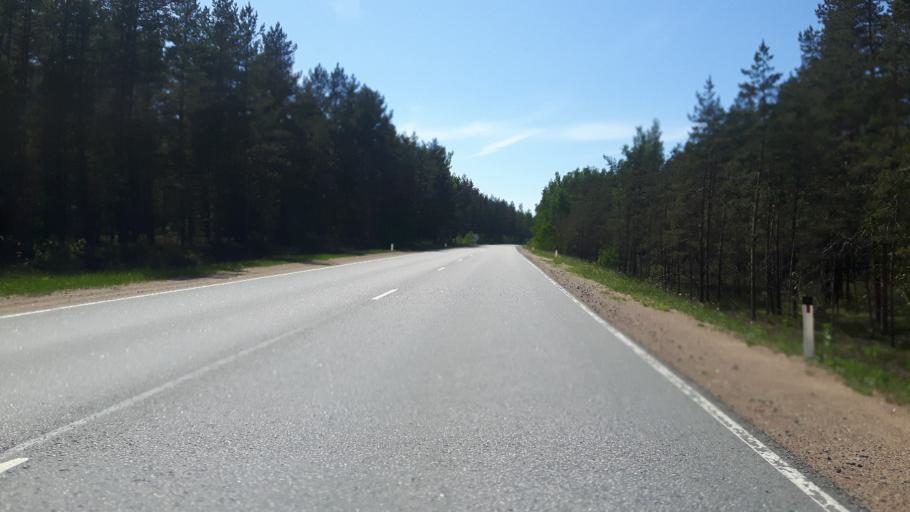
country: RU
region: Leningrad
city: Sista-Palkino
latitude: 59.7667
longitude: 28.7435
